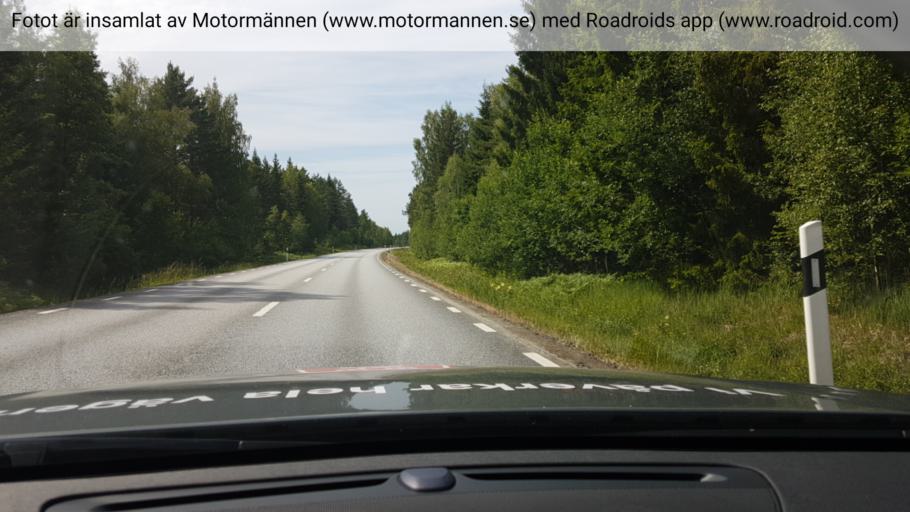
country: SE
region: Uppsala
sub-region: Osthammars Kommun
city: Anneberg
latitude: 60.1746
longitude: 18.4238
